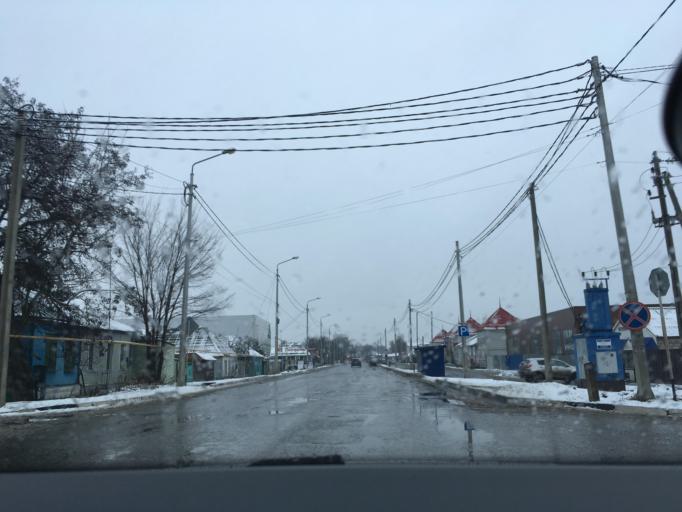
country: RU
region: Belgorod
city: Valuyki
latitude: 50.2022
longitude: 38.1165
